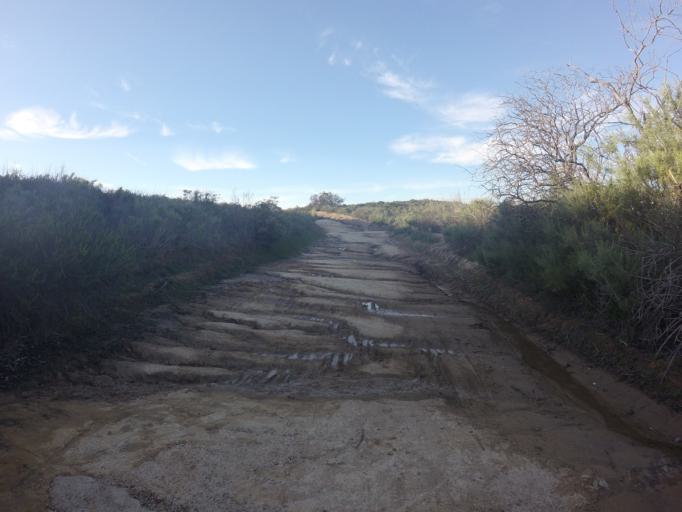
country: US
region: California
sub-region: Orange County
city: Laguna Beach
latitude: 33.5910
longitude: -117.7772
